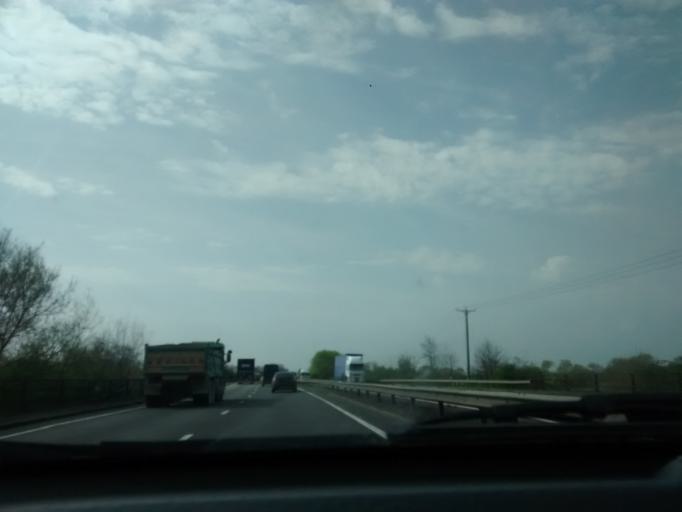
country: GB
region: England
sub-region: Oxfordshire
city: Kidlington
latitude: 51.8211
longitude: -1.2636
